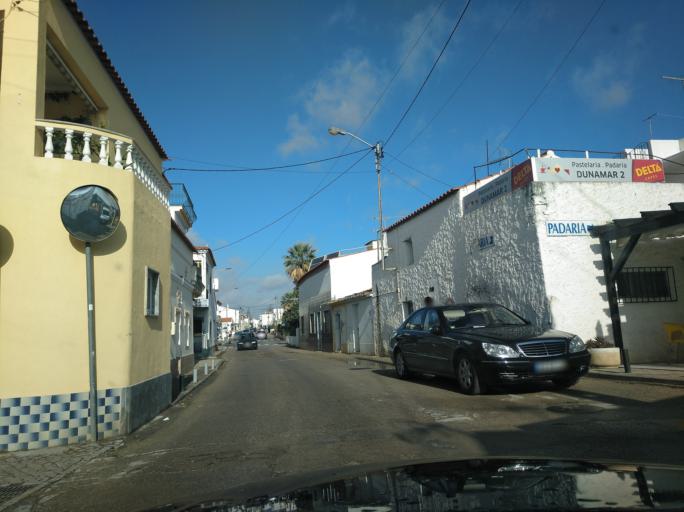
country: PT
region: Faro
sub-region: Vila Real de Santo Antonio
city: Monte Gordo
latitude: 37.1784
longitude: -7.5010
